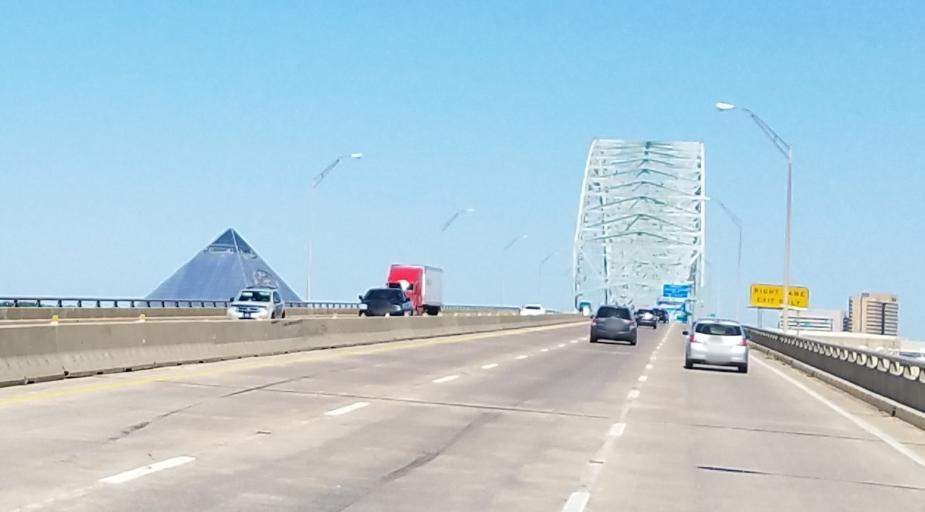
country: US
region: Tennessee
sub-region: Shelby County
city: Memphis
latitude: 35.1487
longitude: -90.0687
